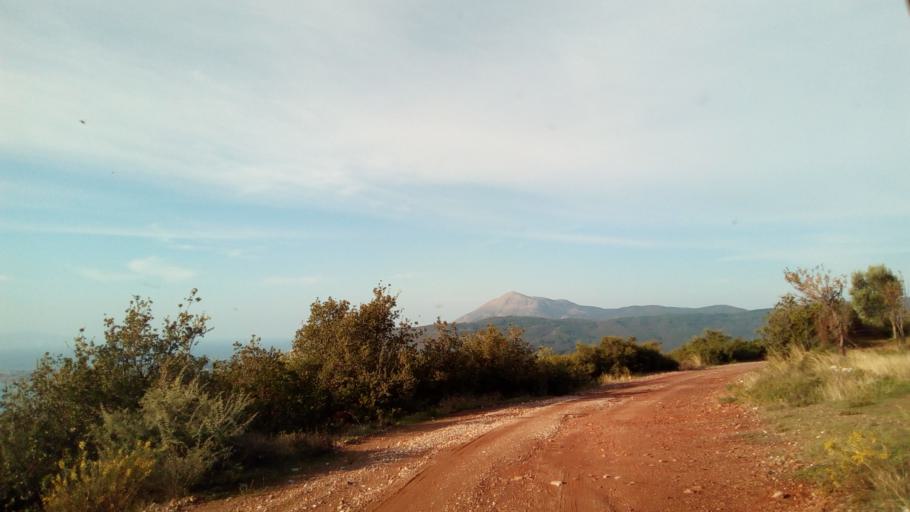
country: GR
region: West Greece
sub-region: Nomos Aitolias kai Akarnanias
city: Nafpaktos
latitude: 38.4082
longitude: 21.8199
